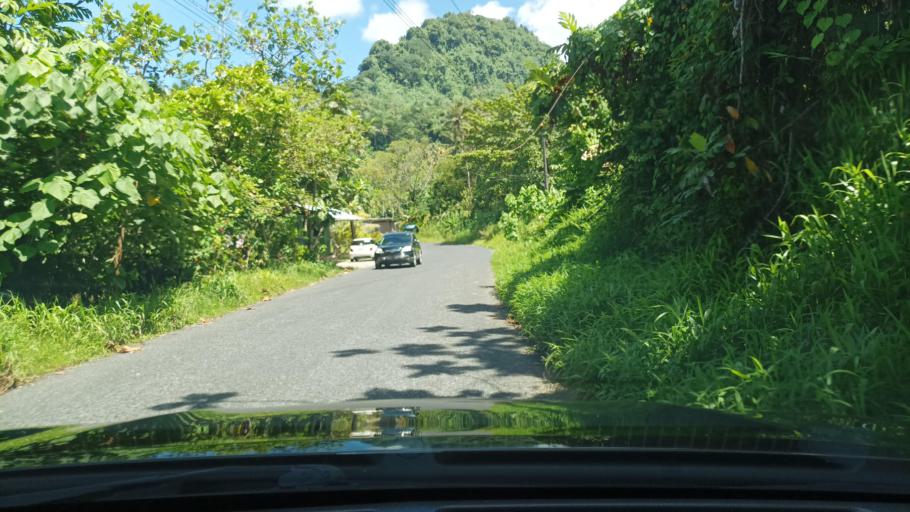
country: FM
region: Pohnpei
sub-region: Kolonia Municipality
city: Kolonia
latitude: 6.9633
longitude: 158.2616
